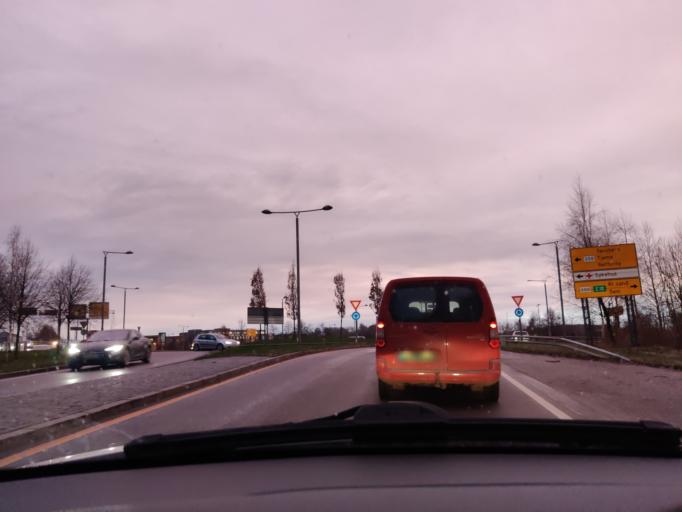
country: NO
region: Vestfold
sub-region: Tonsberg
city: Tonsberg
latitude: 59.2820
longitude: 10.3984
